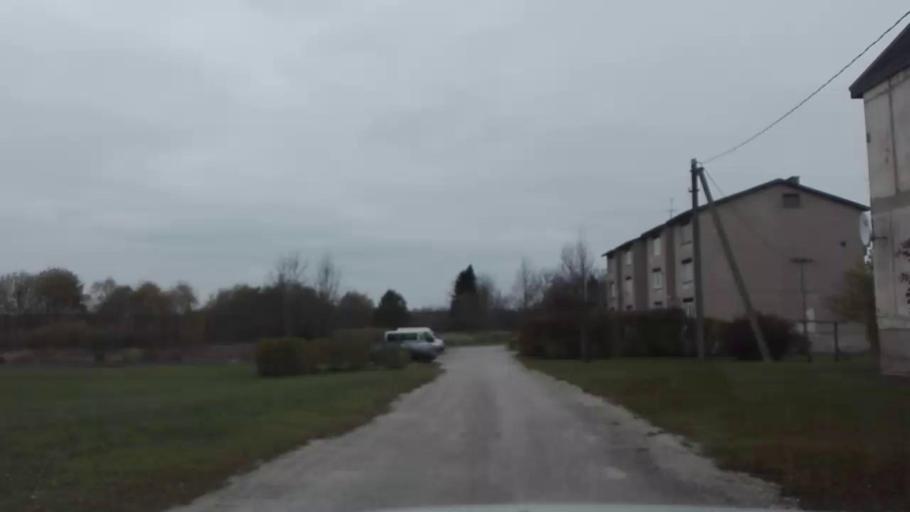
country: EE
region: Jogevamaa
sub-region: Poltsamaa linn
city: Poltsamaa
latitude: 58.4264
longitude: 26.0288
